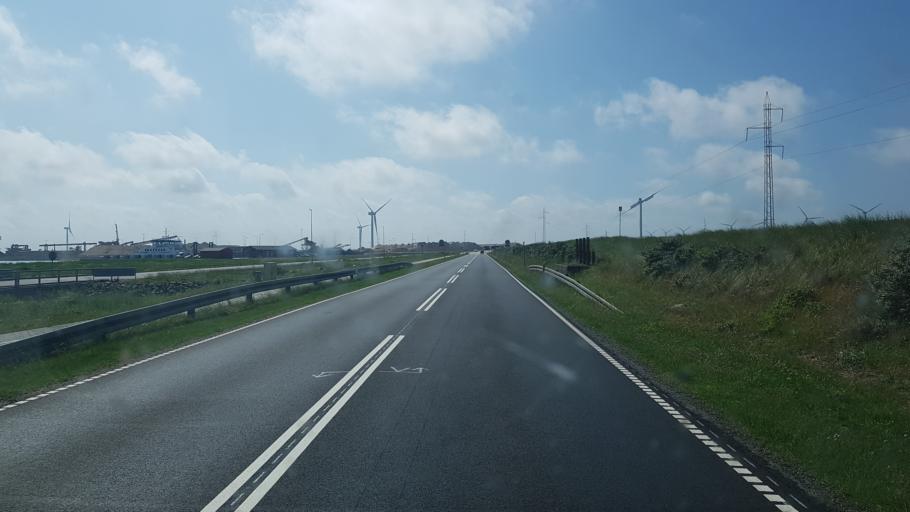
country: DK
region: Central Jutland
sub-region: Lemvig Kommune
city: Thyboron
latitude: 56.6866
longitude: 8.2219
